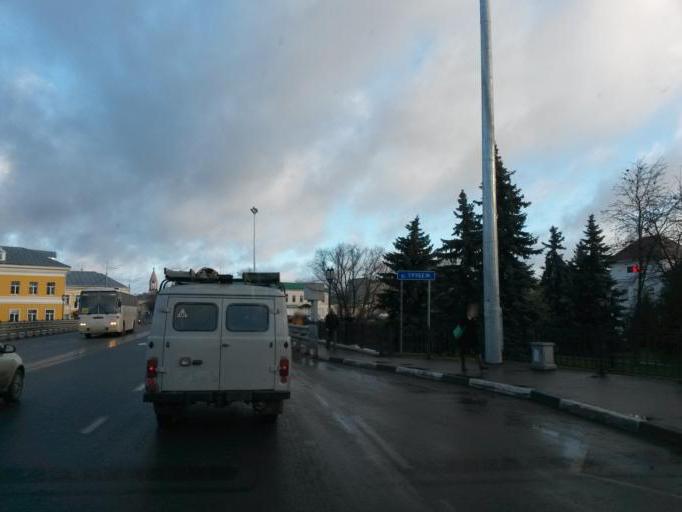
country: RU
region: Jaroslavl
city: Pereslavl'-Zalesskiy
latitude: 56.7379
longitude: 38.8554
